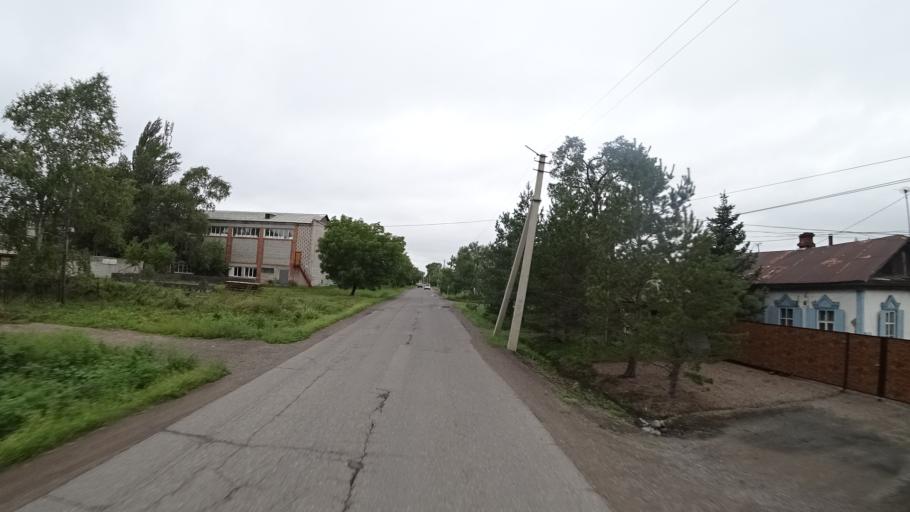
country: RU
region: Primorskiy
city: Chernigovka
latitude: 44.3384
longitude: 132.5788
